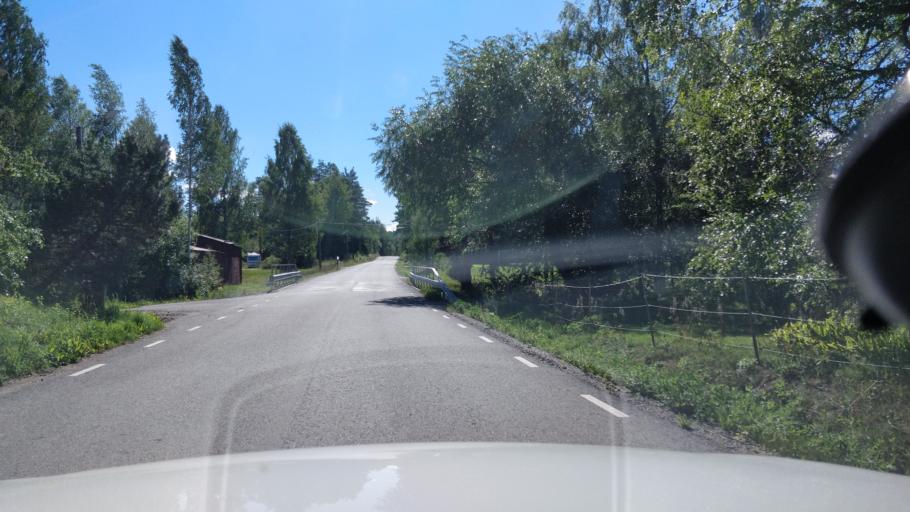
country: SE
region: Dalarna
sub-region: Faluns Kommun
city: Bjursas
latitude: 60.7510
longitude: 15.4807
